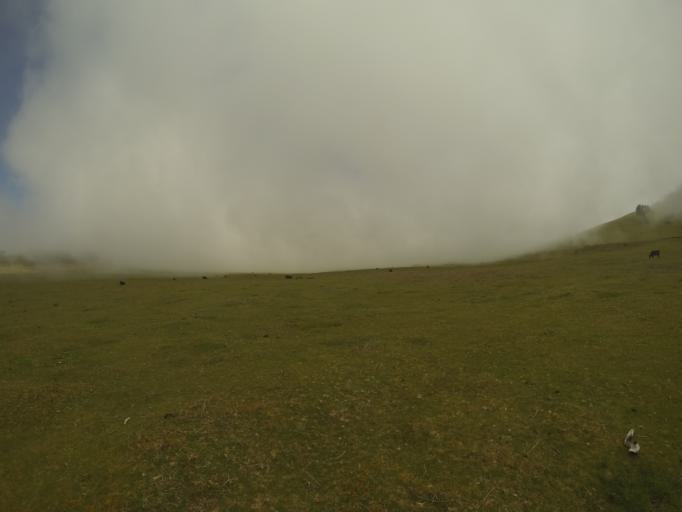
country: PT
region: Madeira
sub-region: Porto Moniz
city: Porto Moniz
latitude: 32.8127
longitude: -17.1450
